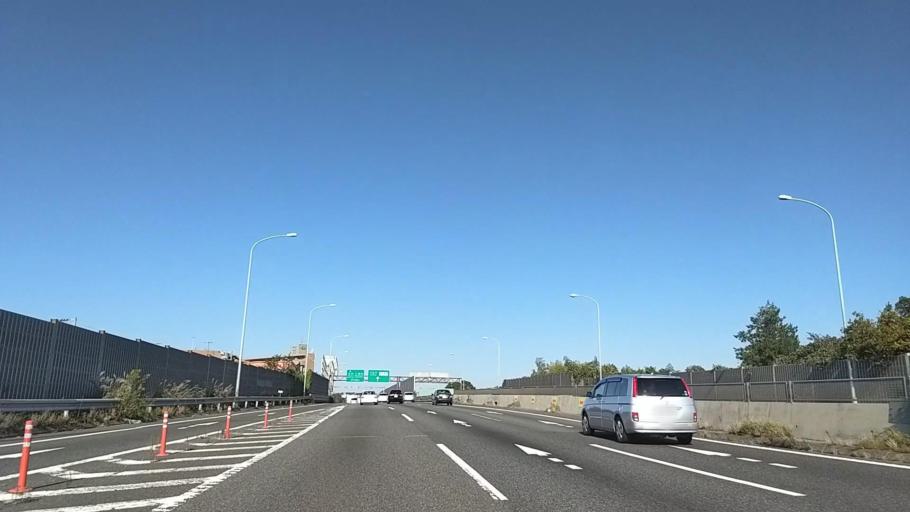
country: JP
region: Kanagawa
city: Minami-rinkan
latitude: 35.4632
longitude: 139.5411
